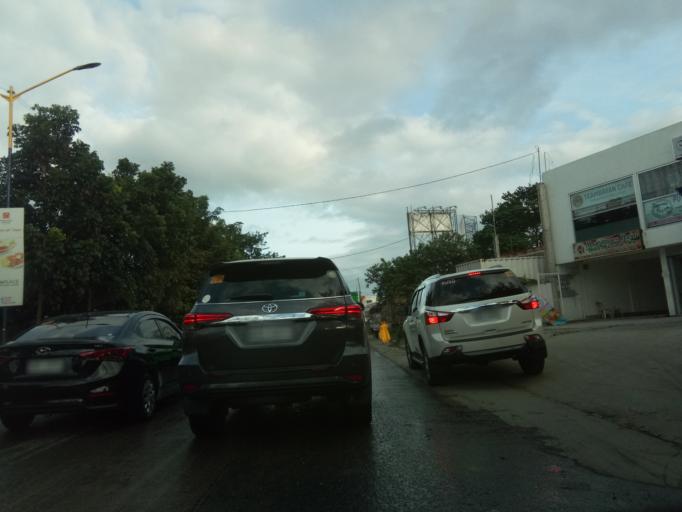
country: PH
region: Calabarzon
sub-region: Province of Cavite
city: Imus
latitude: 14.3864
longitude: 120.9761
